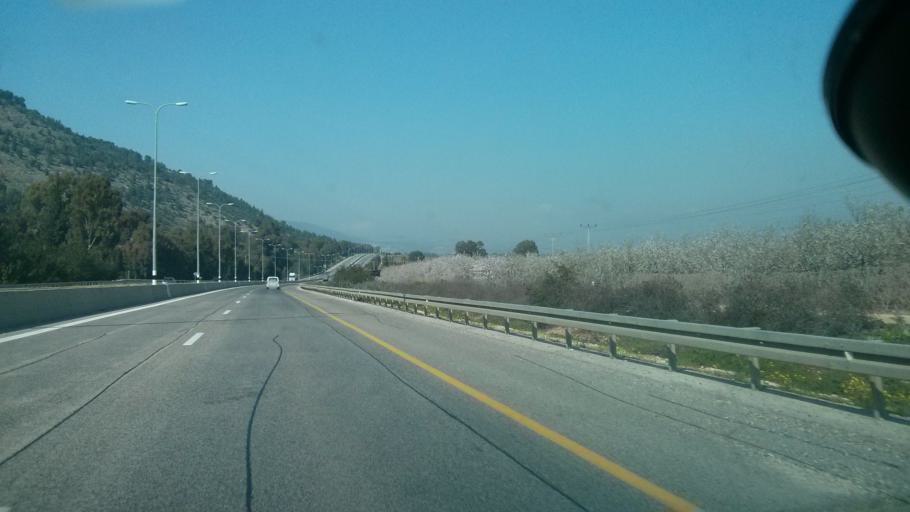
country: IL
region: Northern District
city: Rosh Pinna
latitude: 33.0790
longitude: 35.5755
